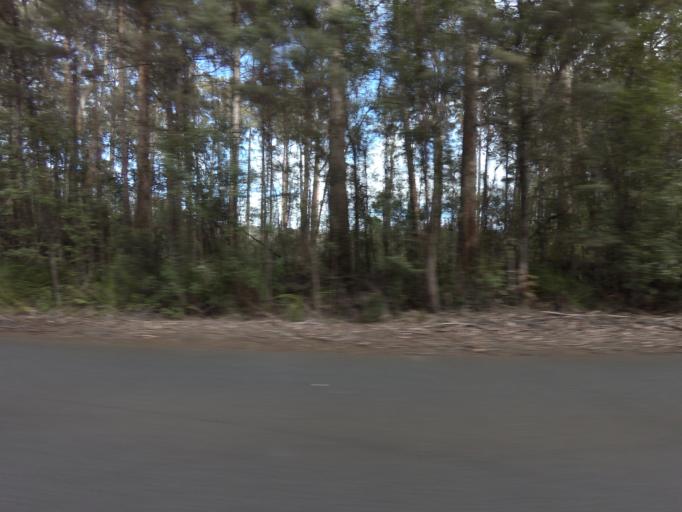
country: AU
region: Tasmania
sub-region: Huon Valley
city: Geeveston
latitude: -43.3835
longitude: 146.9616
